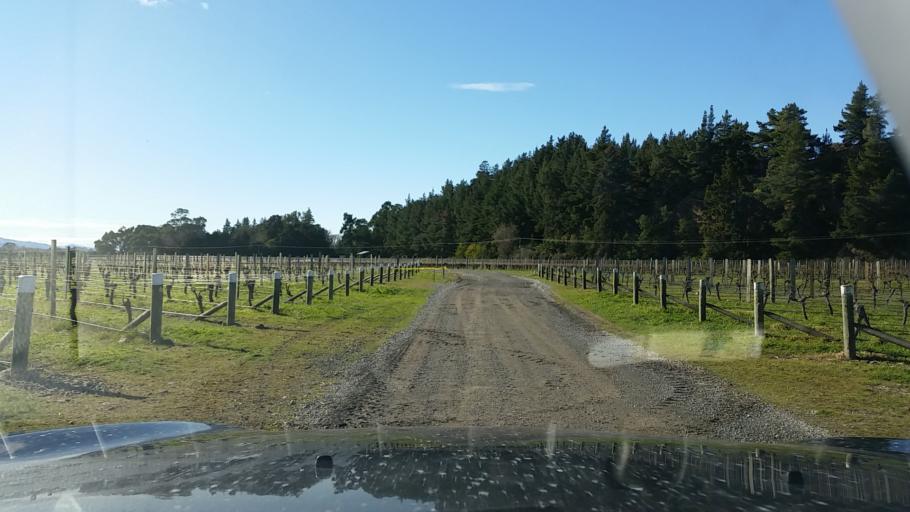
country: NZ
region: Marlborough
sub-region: Marlborough District
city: Blenheim
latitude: -41.5297
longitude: 173.8033
